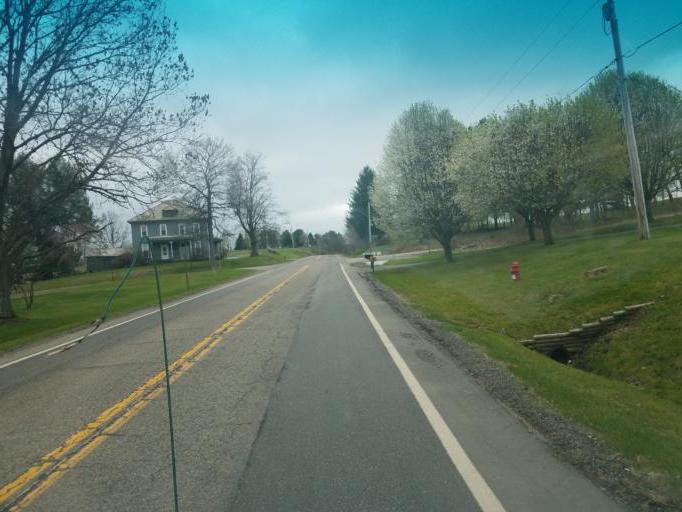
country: US
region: Ohio
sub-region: Stark County
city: Beach City
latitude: 40.5921
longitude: -81.6039
